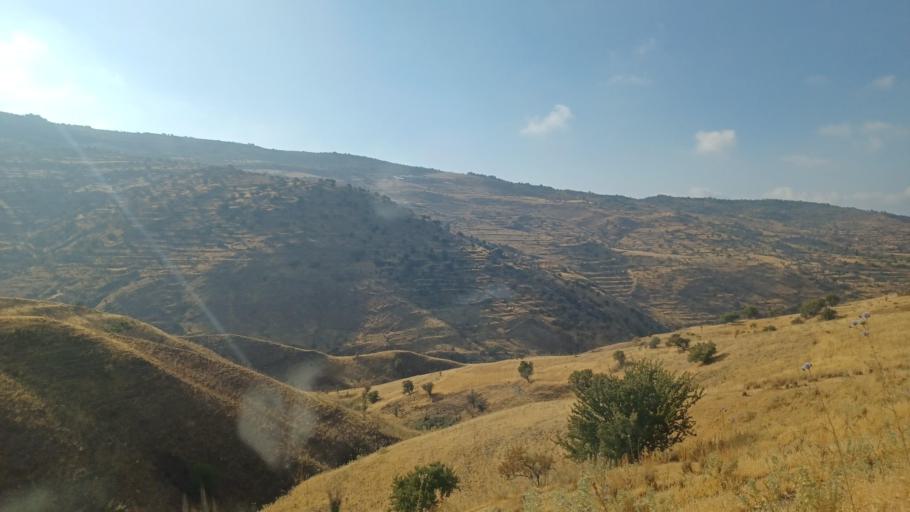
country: CY
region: Pafos
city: Mesogi
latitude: 34.8645
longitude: 32.6013
